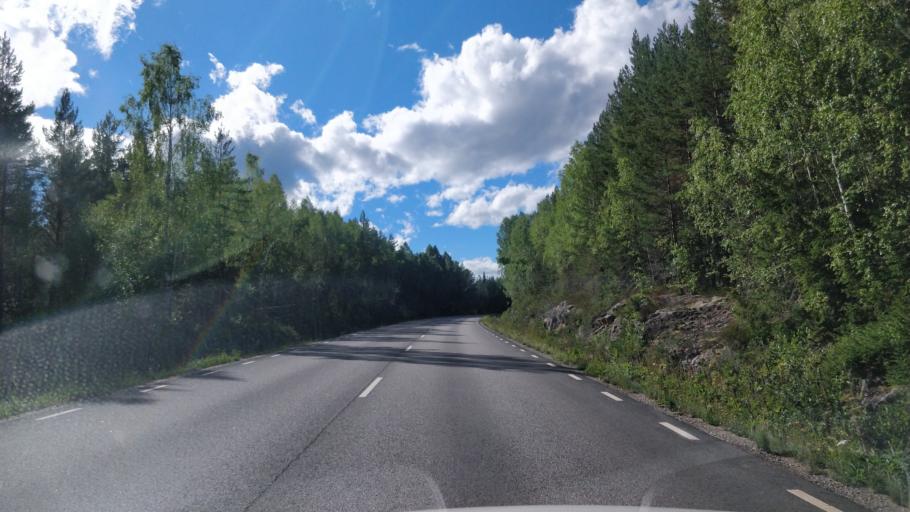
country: SE
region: Dalarna
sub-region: Ludvika Kommun
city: Ludvika
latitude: 60.2906
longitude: 15.2385
